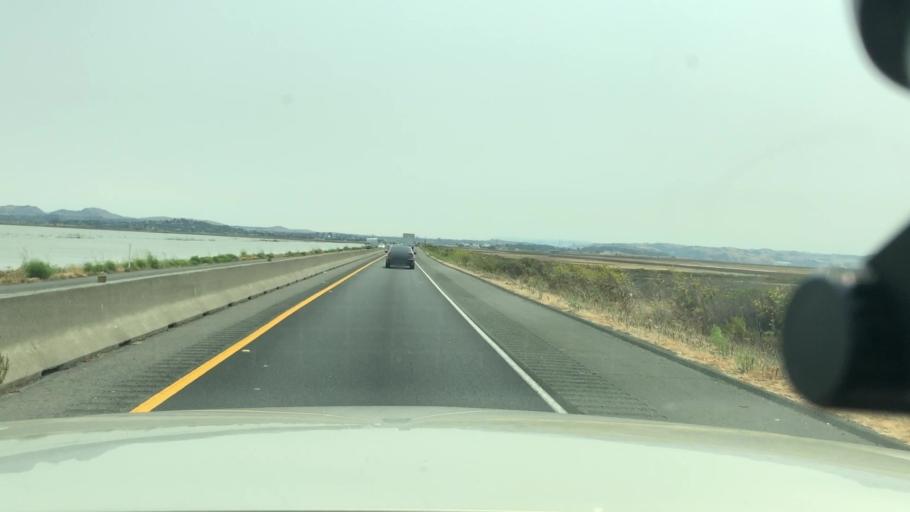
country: US
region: California
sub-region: Solano County
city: Vallejo
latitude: 38.1281
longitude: -122.3272
